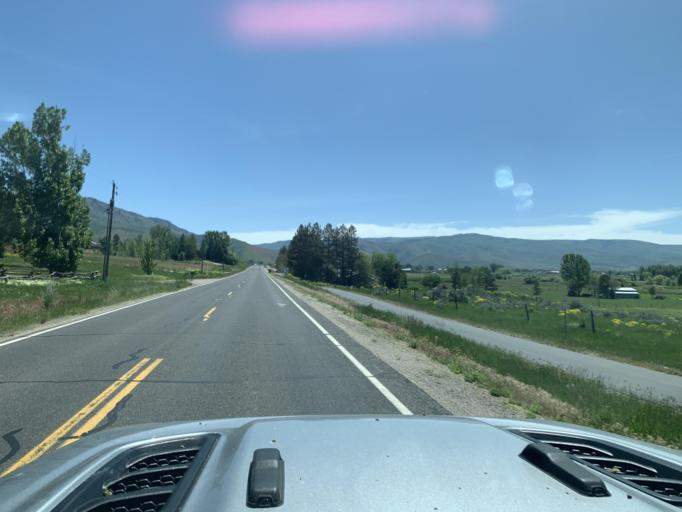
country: US
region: Utah
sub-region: Weber County
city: Wolf Creek
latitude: 41.2676
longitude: -111.7727
